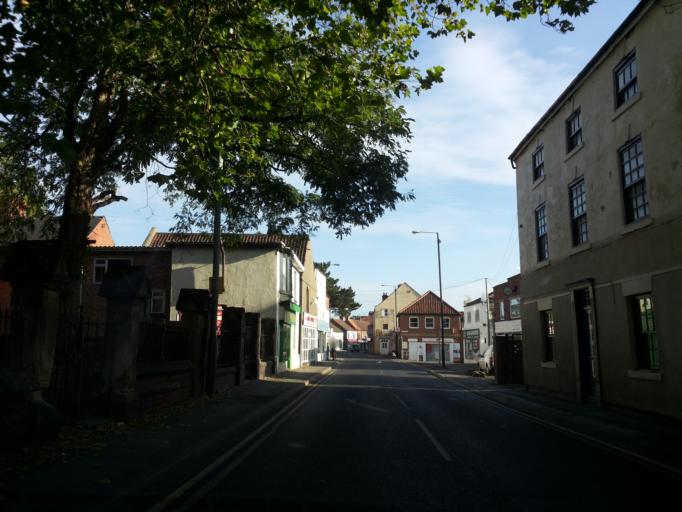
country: GB
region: England
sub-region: Doncaster
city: Hatfield
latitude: 53.6123
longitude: -0.9631
